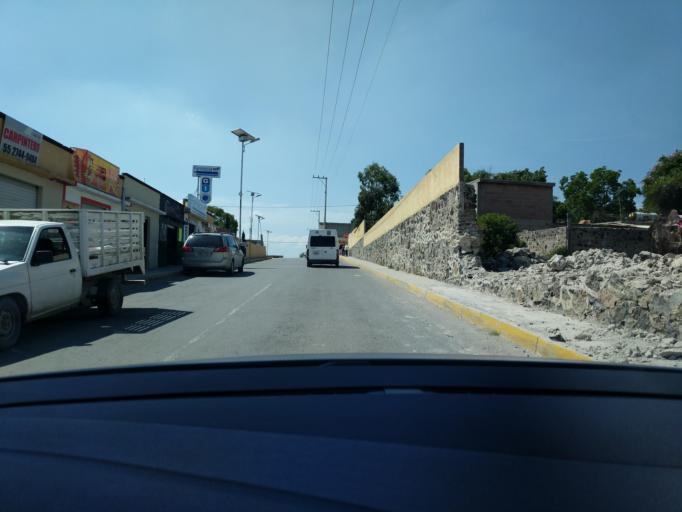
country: MX
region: Hidalgo
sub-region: Atotonilco de Tula
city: Paseos de la Pradera
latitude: 19.9326
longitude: -99.2339
